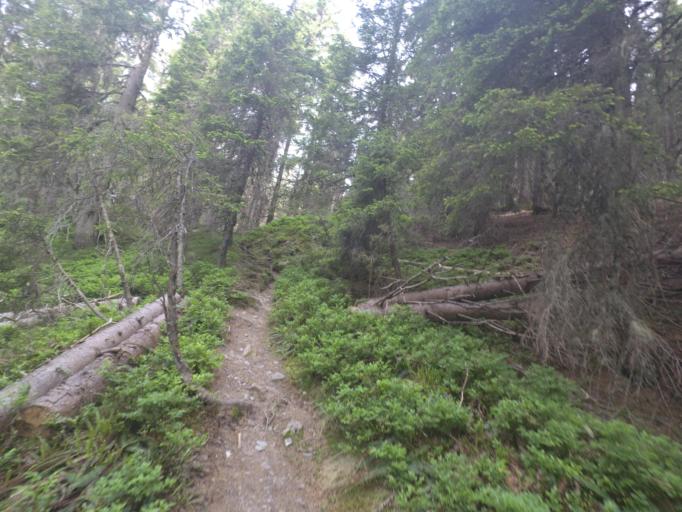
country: AT
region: Salzburg
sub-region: Politischer Bezirk Sankt Johann im Pongau
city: Muhlbach am Hochkonig
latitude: 47.3664
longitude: 13.0873
